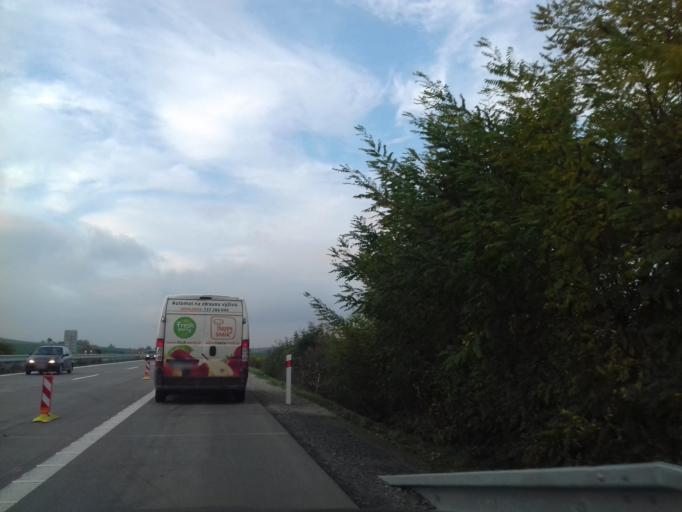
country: CZ
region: South Moravian
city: Nosislav
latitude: 49.0348
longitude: 16.6824
